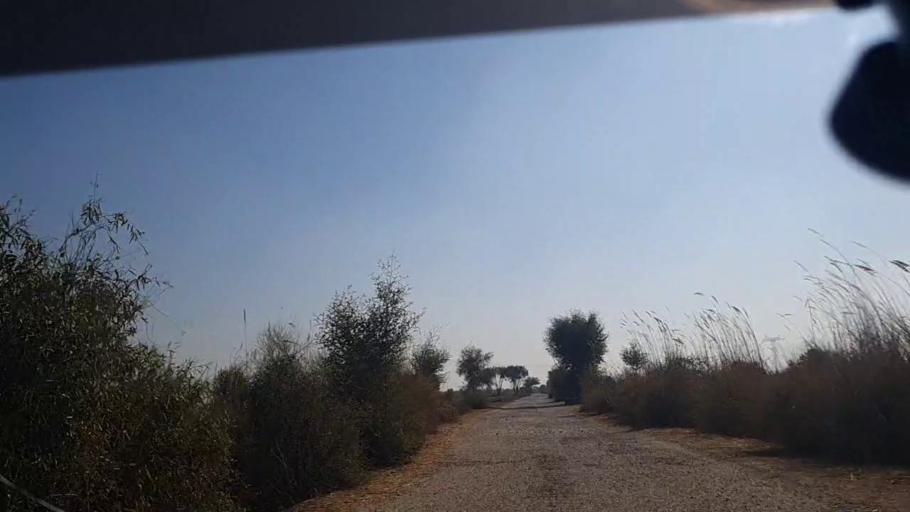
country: PK
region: Sindh
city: Khanpur
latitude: 27.5847
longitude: 69.3049
